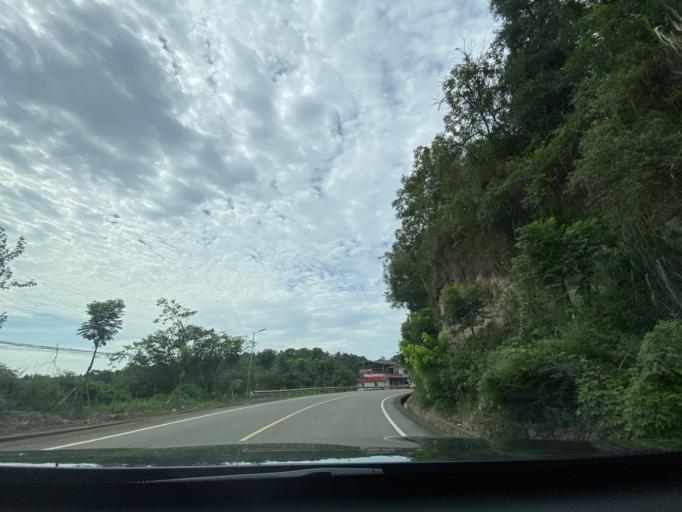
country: CN
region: Sichuan
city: Jiancheng
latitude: 30.4755
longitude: 104.6298
